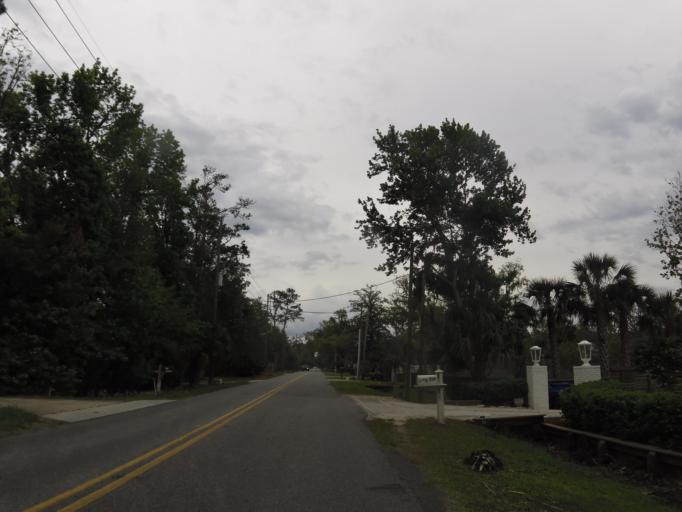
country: US
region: Florida
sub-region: Saint Johns County
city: Palm Valley
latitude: 30.2056
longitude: -81.4075
